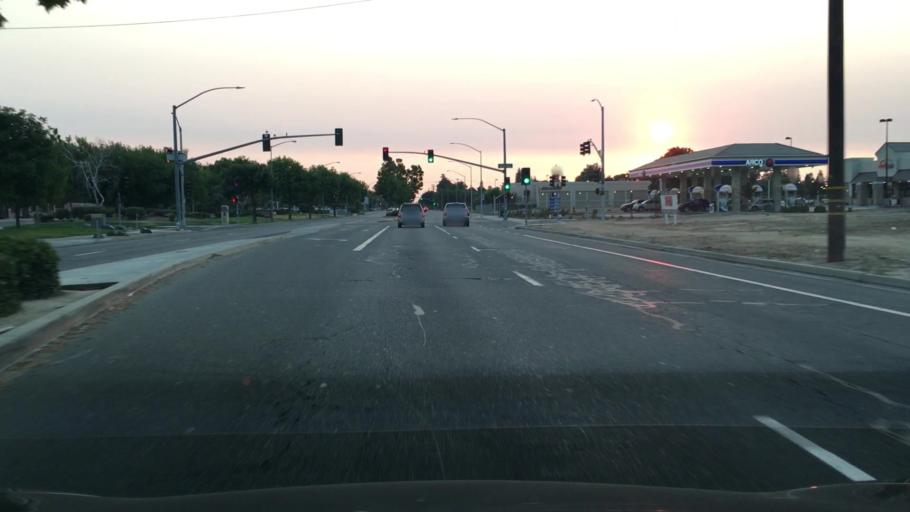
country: US
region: California
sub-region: Fresno County
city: Clovis
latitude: 36.8520
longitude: -119.7694
